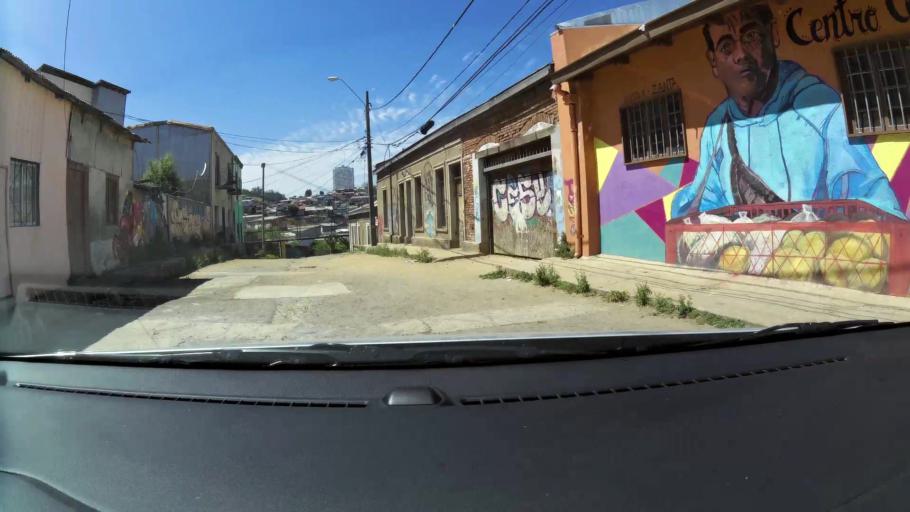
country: CL
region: Valparaiso
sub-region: Provincia de Valparaiso
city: Valparaiso
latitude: -33.0499
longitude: -71.5990
